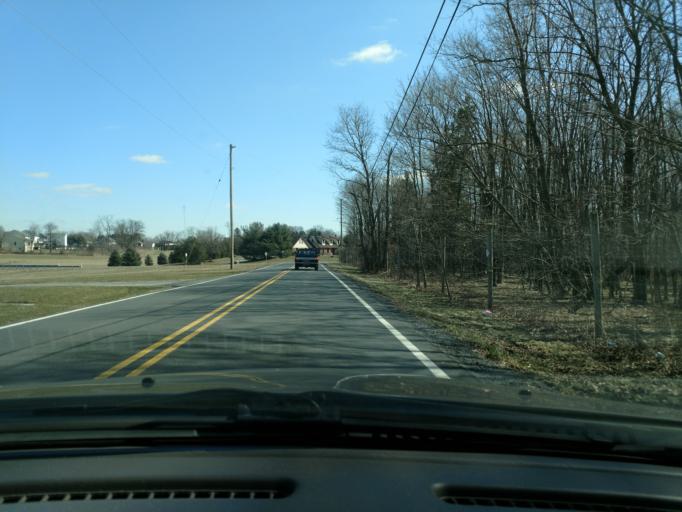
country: US
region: Pennsylvania
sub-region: Lebanon County
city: Sand Hill
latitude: 40.3658
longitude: -76.4390
